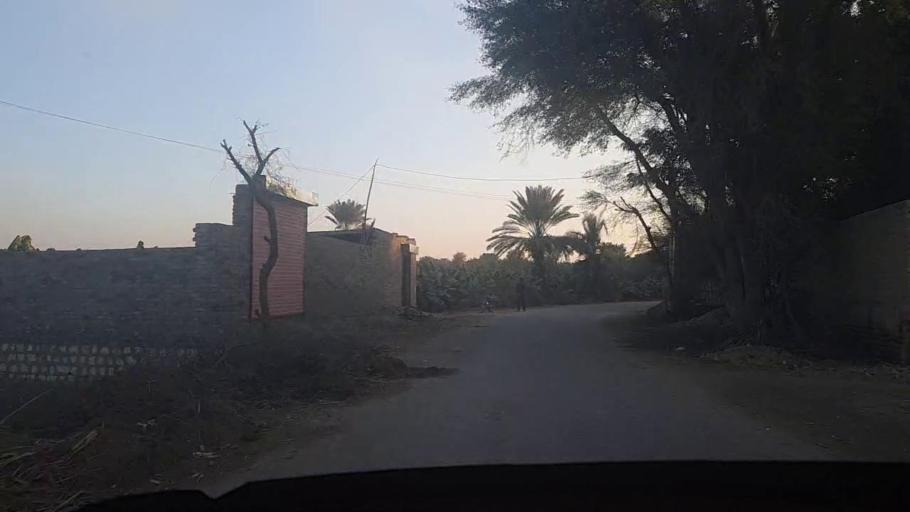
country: PK
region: Sindh
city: Sobhadero
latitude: 27.3394
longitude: 68.3789
